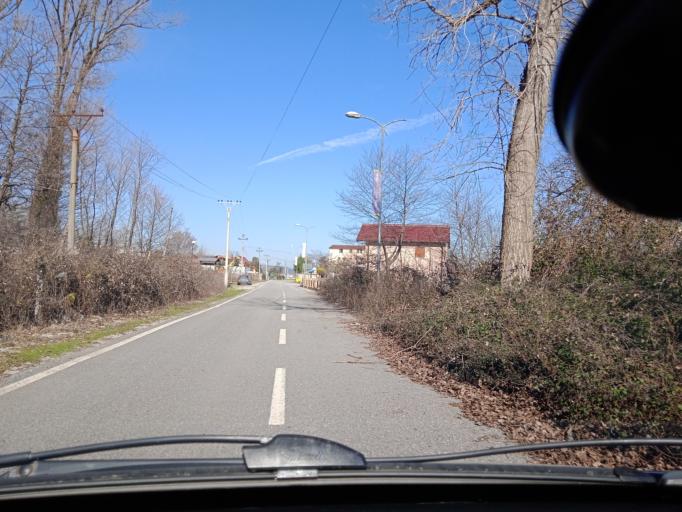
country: AL
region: Shkoder
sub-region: Rrethi i Shkodres
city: Velipoje
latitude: 41.8653
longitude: 19.4063
